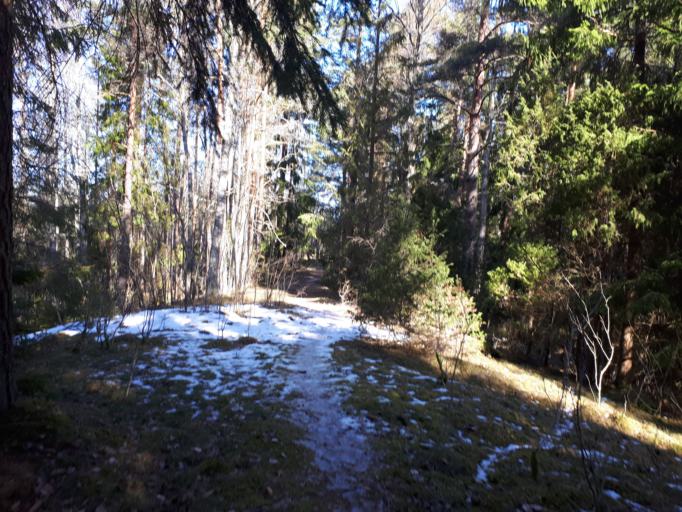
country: SE
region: Soedermanland
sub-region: Flens Kommun
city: Halleforsnas
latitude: 59.0832
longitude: 16.3659
